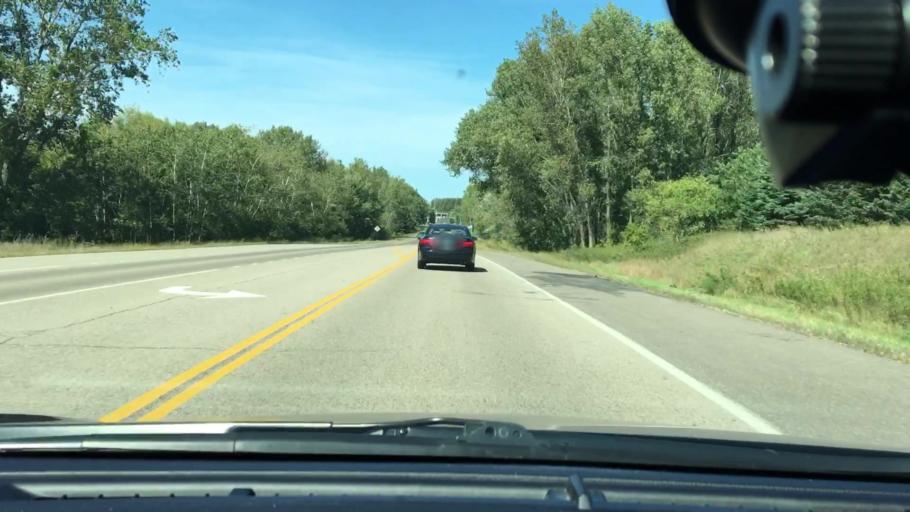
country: US
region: Minnesota
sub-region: Washington County
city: Mahtomedi
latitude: 45.0514
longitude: -92.9475
